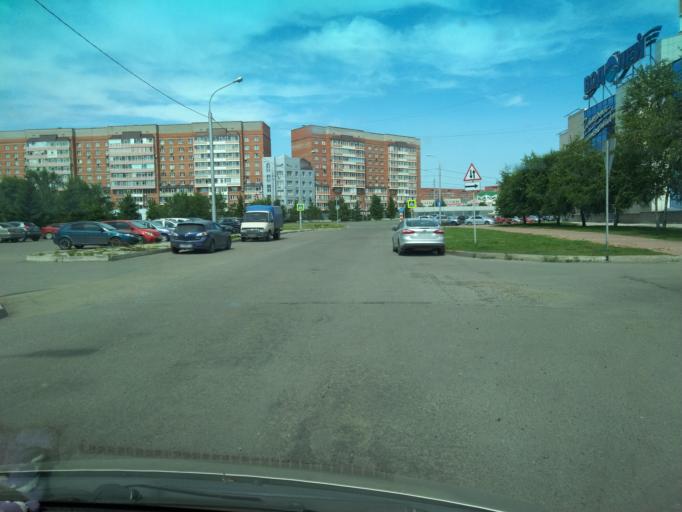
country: RU
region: Krasnoyarskiy
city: Krasnoyarsk
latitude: 56.0505
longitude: 92.9129
